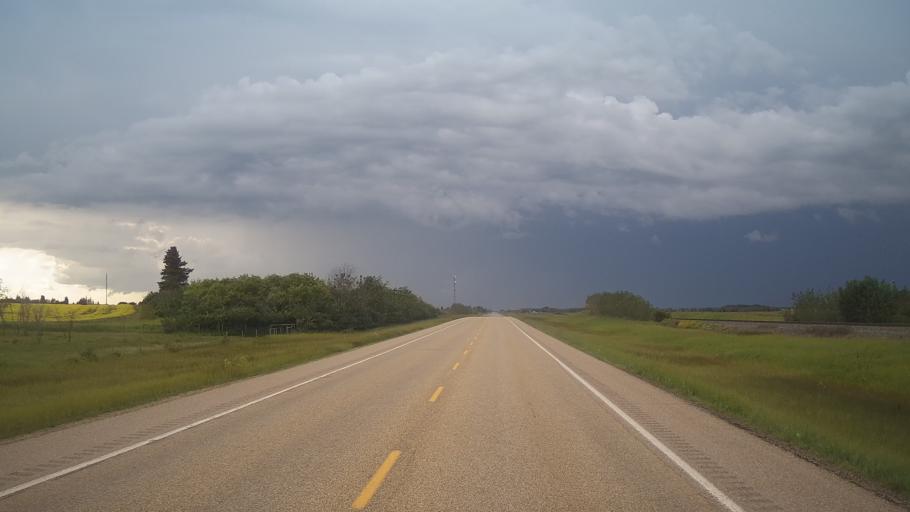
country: CA
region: Alberta
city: Tofield
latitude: 53.2651
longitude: -112.3540
